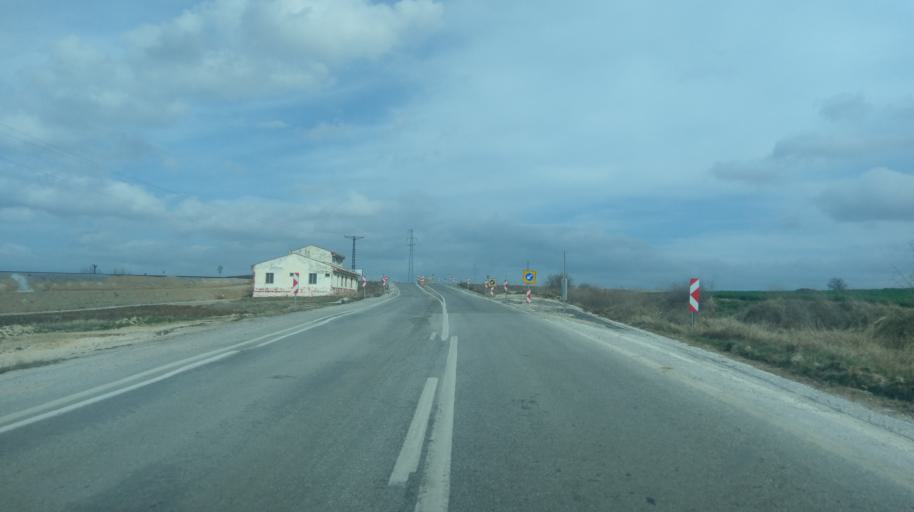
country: TR
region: Kirklareli
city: Inece
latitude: 41.6796
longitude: 27.0944
